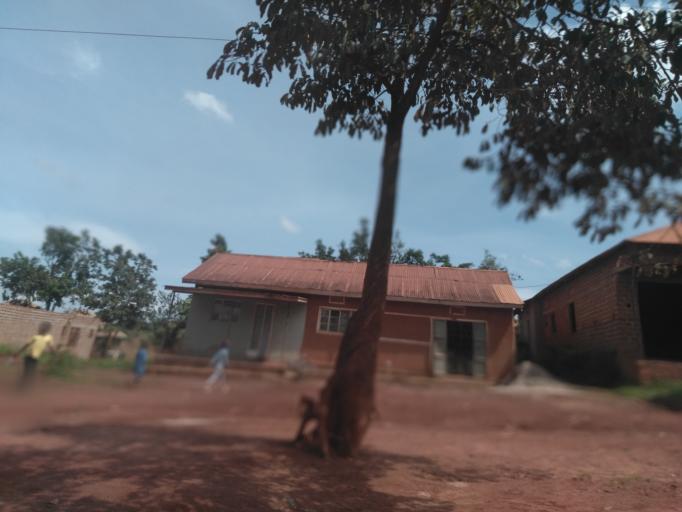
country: UG
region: Central Region
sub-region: Wakiso District
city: Kireka
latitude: 0.4407
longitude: 32.5976
